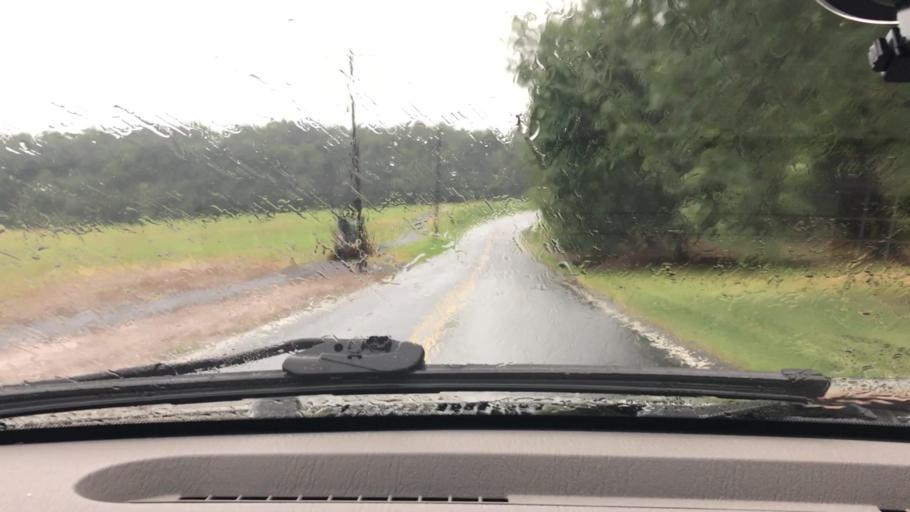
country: US
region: Pennsylvania
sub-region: Lancaster County
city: Elizabethtown
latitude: 40.1323
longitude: -76.6155
